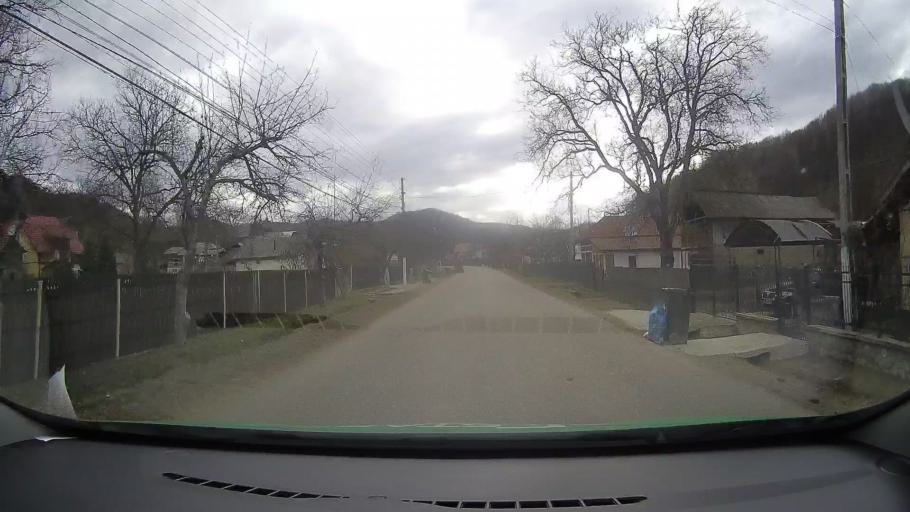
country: RO
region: Dambovita
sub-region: Comuna Visinesti
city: Visinesti
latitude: 45.1004
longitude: 25.5665
